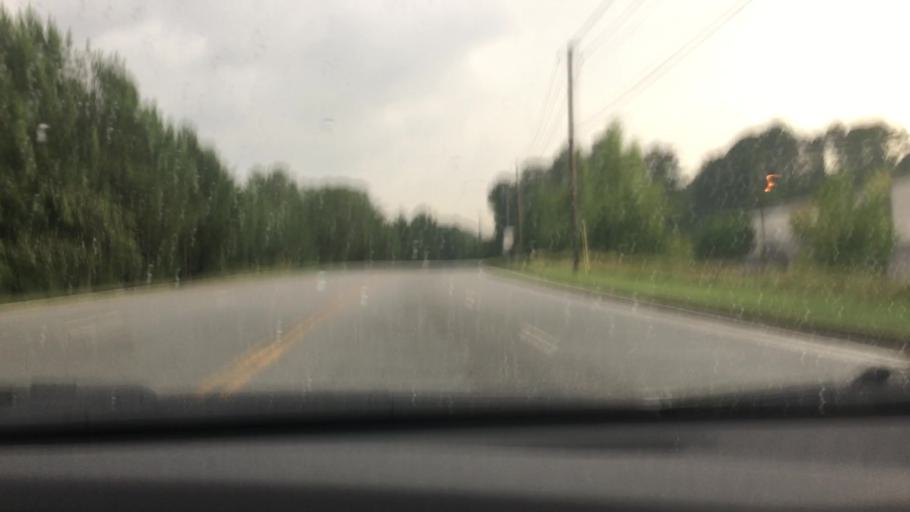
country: US
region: Georgia
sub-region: Fulton County
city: Union City
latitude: 33.6426
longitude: -84.5227
